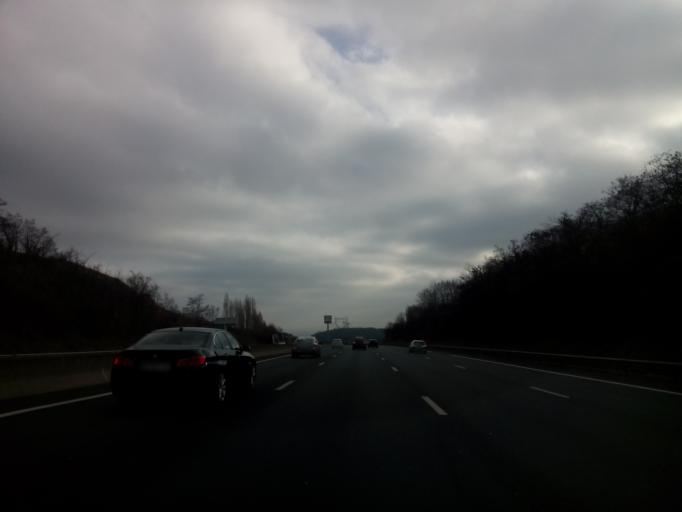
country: FR
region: Rhone-Alpes
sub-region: Departement de l'Isere
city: Grenay
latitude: 45.6591
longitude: 5.0766
